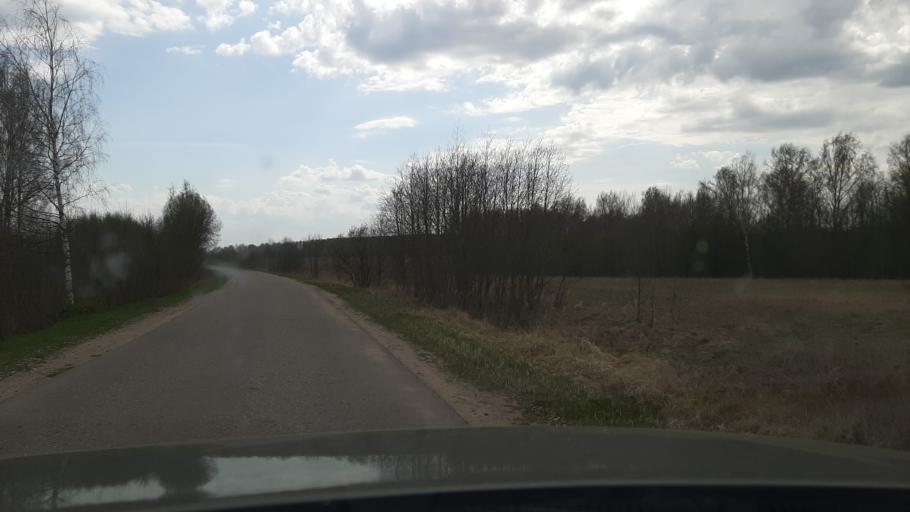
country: RU
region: Ivanovo
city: Furmanov
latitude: 57.3085
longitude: 41.1616
